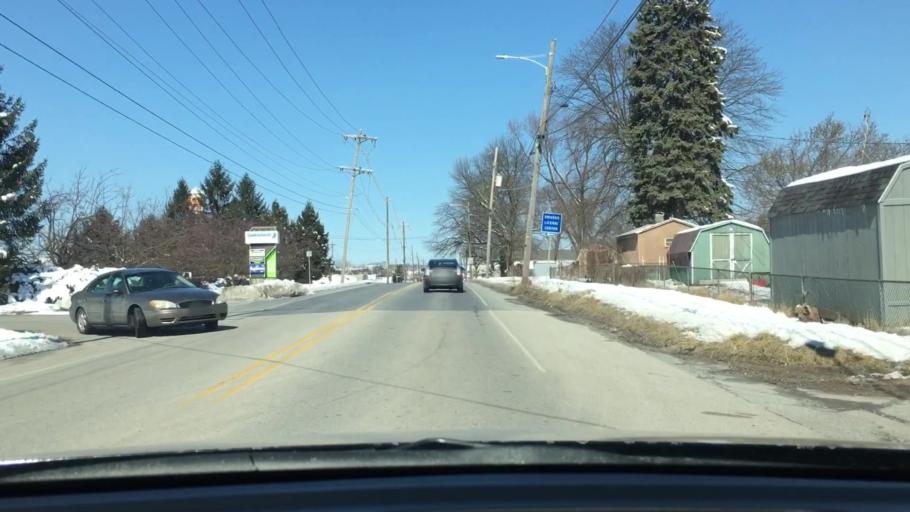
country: US
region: Pennsylvania
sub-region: York County
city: West York
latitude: 39.9729
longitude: -76.7531
